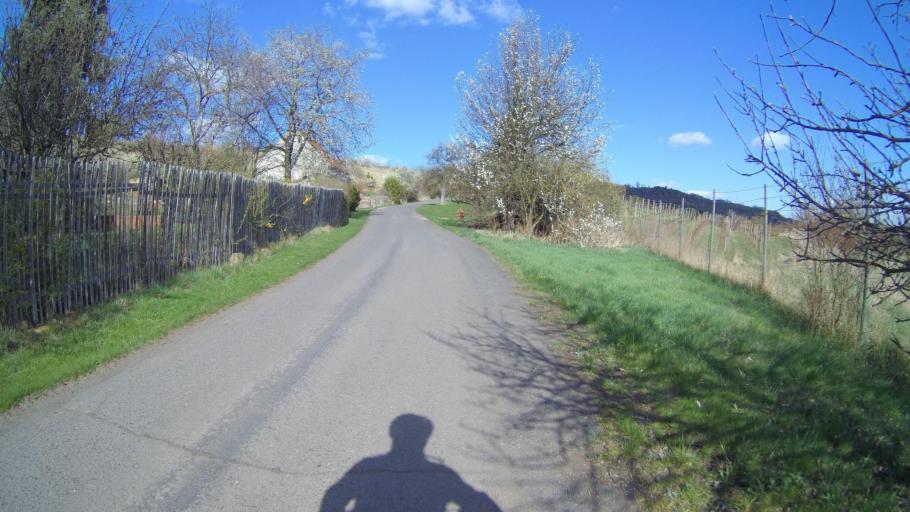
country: CZ
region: Ustecky
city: Brezno
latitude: 50.3701
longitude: 13.4516
